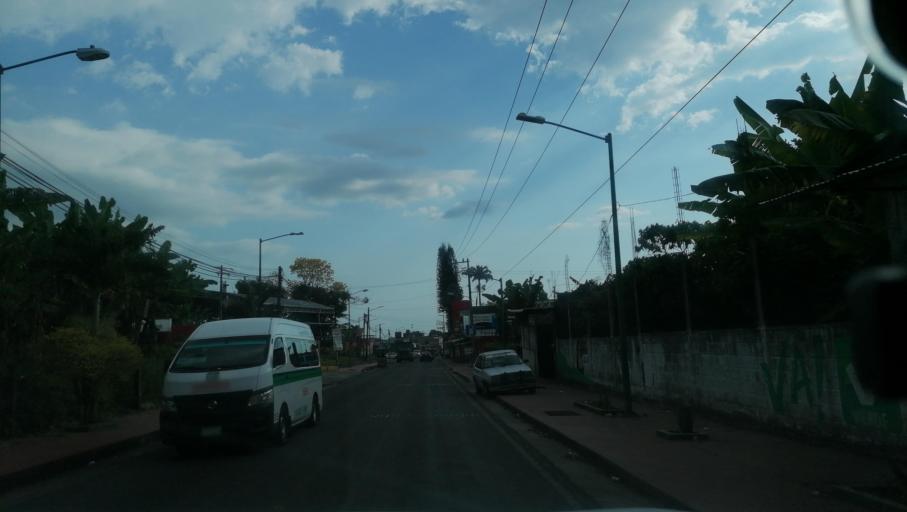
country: MX
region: Chiapas
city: Cacahoatan
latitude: 15.0002
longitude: -92.1630
